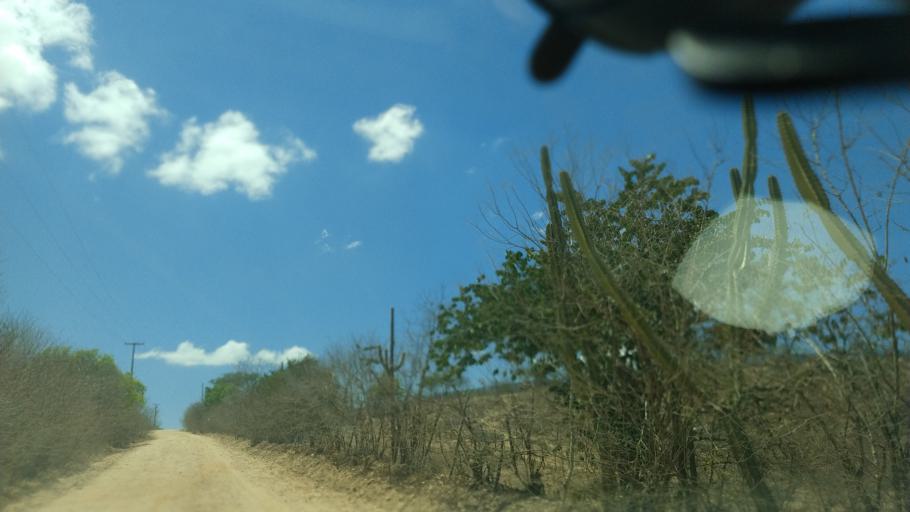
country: BR
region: Rio Grande do Norte
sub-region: Cerro Cora
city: Cerro Cora
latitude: -6.0159
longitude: -36.3285
